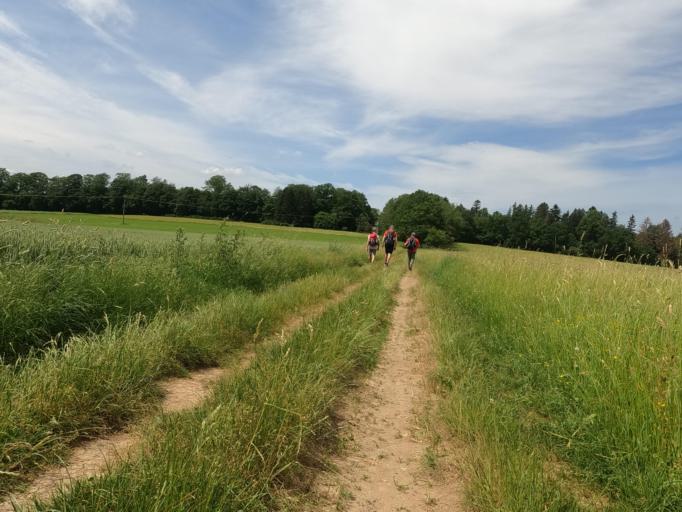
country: DE
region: Rheinland-Pfalz
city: Gehlert
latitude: 50.6462
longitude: 7.8344
